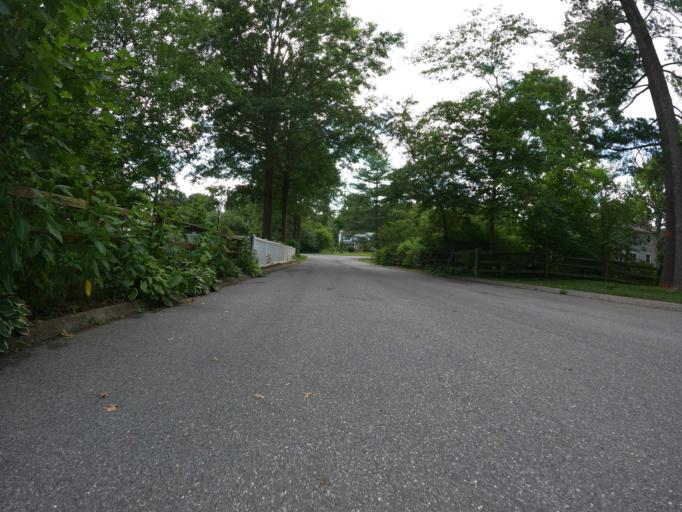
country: US
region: Maryland
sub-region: Howard County
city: Columbia
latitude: 39.2293
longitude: -76.8653
